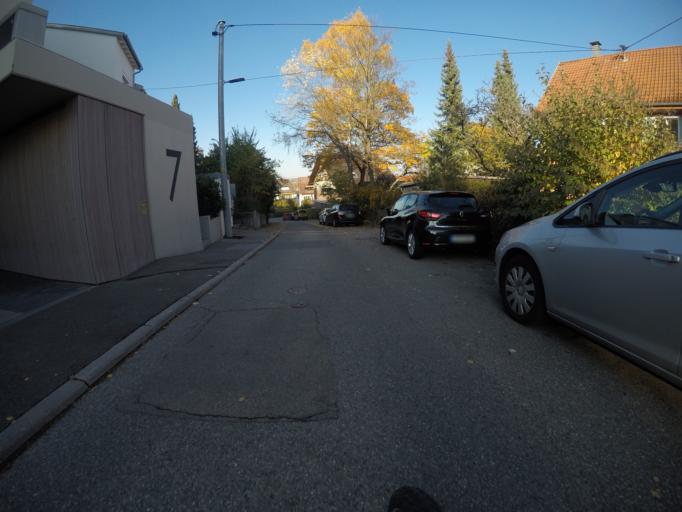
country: DE
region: Baden-Wuerttemberg
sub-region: Regierungsbezirk Stuttgart
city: Steinenbronn
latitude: 48.7195
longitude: 9.1005
